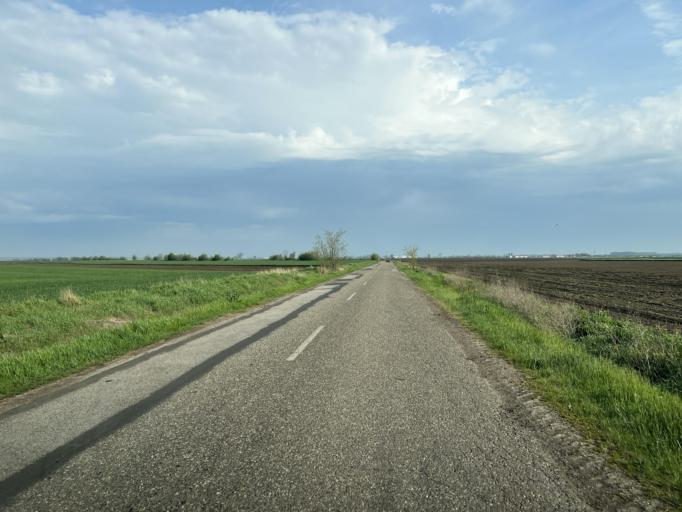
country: HU
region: Pest
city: Tapioszentmarton
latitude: 47.2858
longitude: 19.7632
